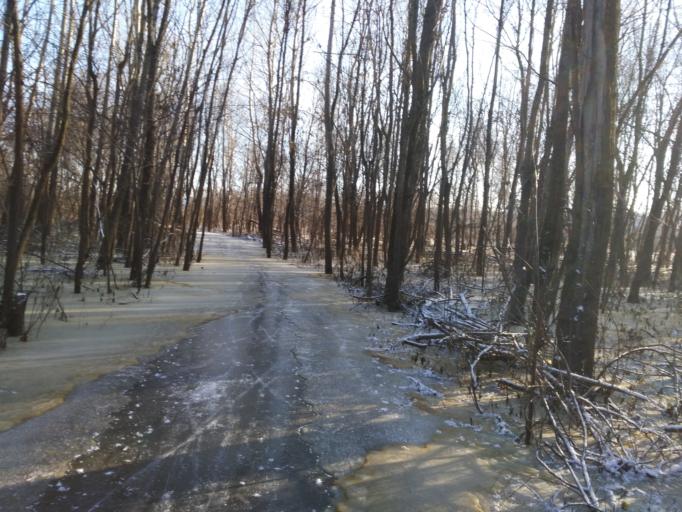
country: RU
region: Kirov
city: Vyatskiye Polyany
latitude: 56.2369
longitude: 51.0820
